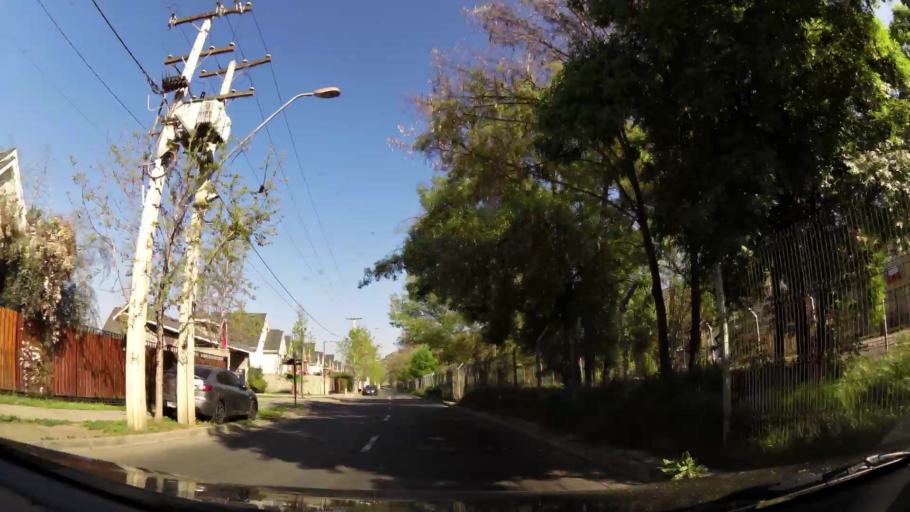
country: CL
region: Santiago Metropolitan
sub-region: Provincia de Chacabuco
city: Chicureo Abajo
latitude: -33.3521
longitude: -70.6798
